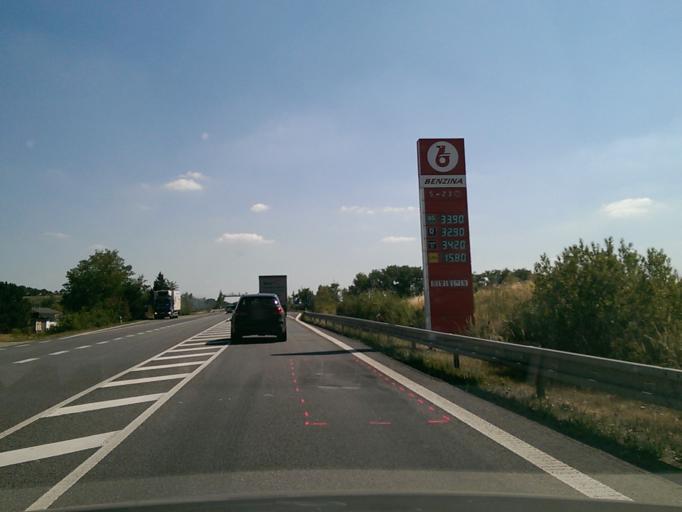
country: CZ
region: South Moravian
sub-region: Okres Breclav
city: Dolni Dunajovice
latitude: 48.8319
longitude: 16.6126
